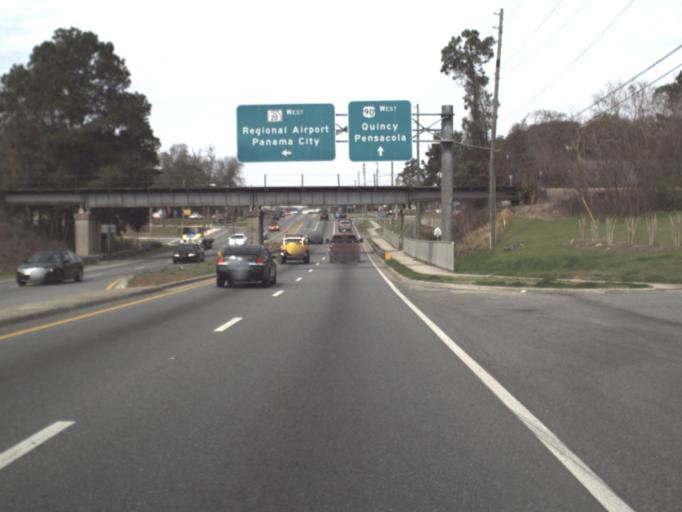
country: US
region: Florida
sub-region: Leon County
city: Tallahassee
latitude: 30.4553
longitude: -84.3427
